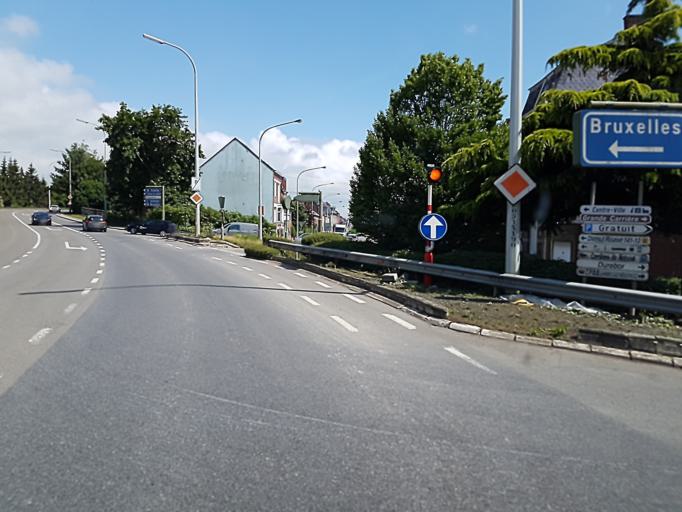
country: BE
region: Wallonia
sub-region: Province du Hainaut
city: Soignies
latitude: 50.5701
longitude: 4.0655
